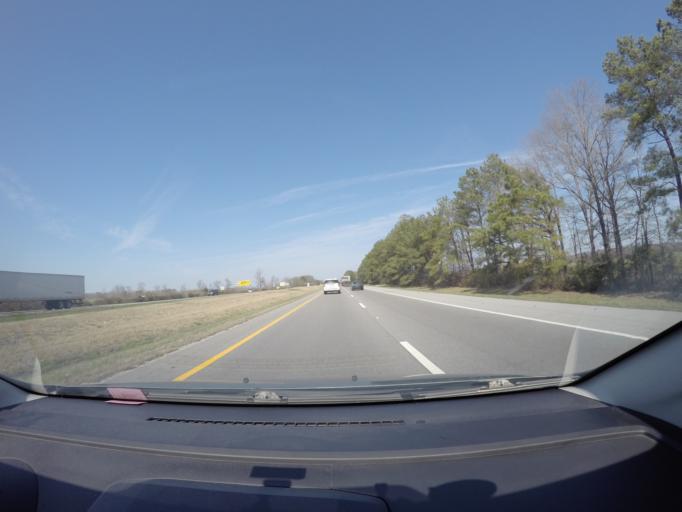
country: US
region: Tennessee
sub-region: Coffee County
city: New Union
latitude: 35.5166
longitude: -86.1204
